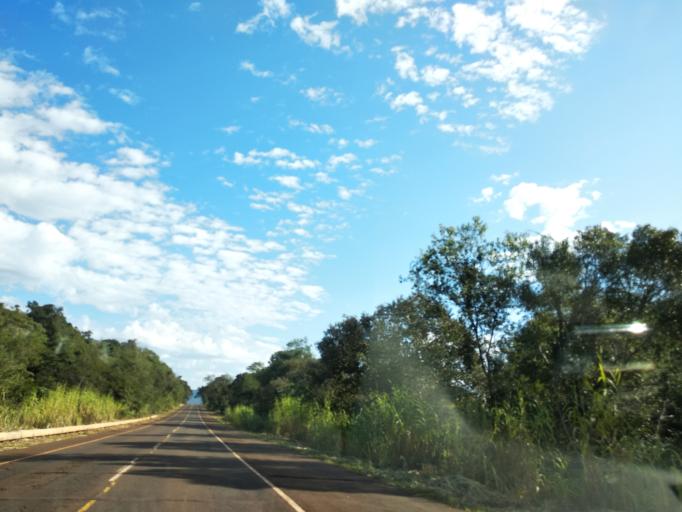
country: AR
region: Misiones
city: Aristobulo del Valle
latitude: -27.0948
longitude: -54.9537
